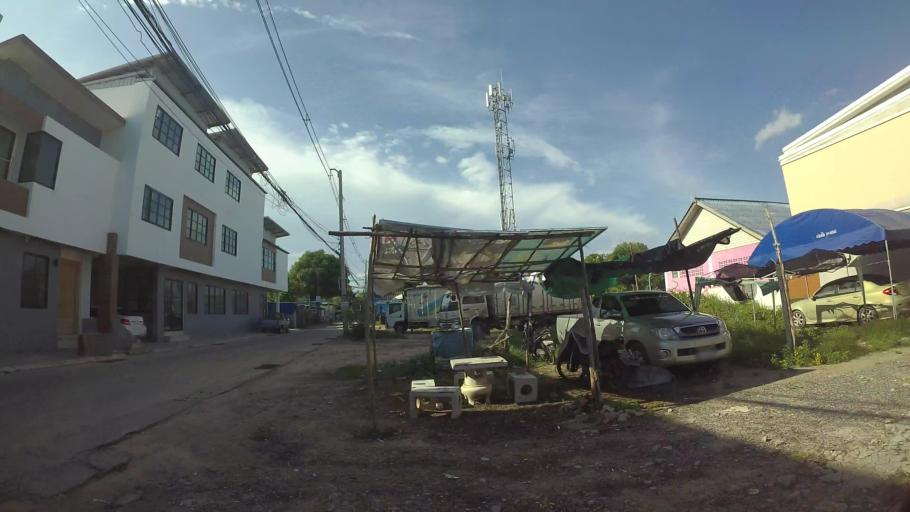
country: TH
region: Rayong
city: Rayong
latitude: 12.6660
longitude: 101.3007
